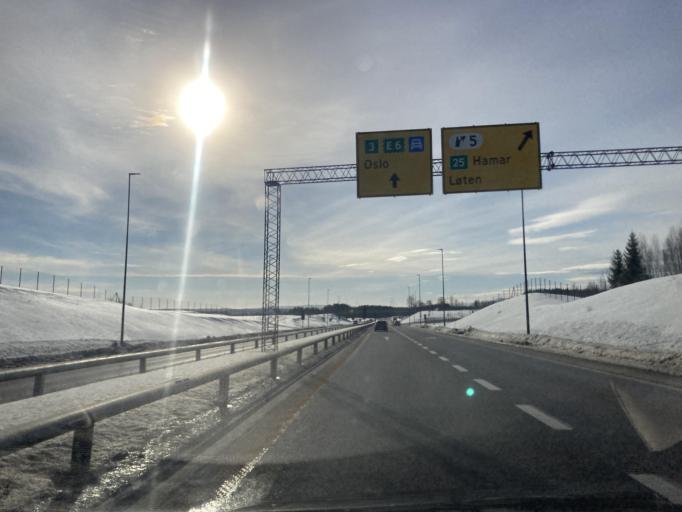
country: NO
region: Hedmark
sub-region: Loten
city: Loten
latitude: 60.8305
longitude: 11.2930
